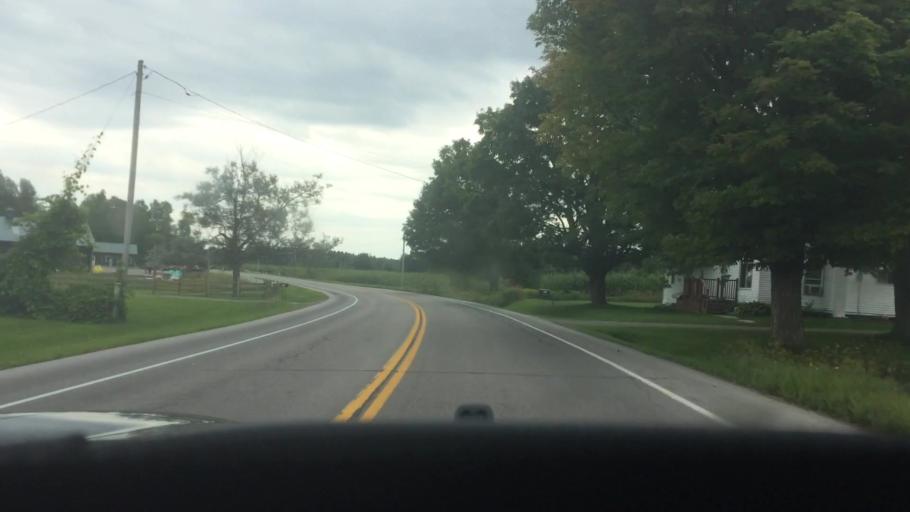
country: US
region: New York
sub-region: St. Lawrence County
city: Ogdensburg
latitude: 44.5842
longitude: -75.3713
